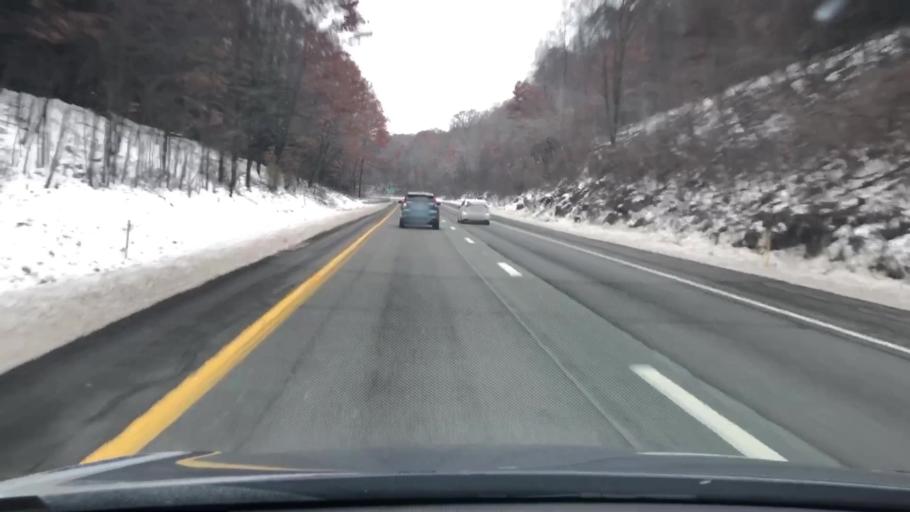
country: US
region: Pennsylvania
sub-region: Jefferson County
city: Reynoldsville
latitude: 41.1415
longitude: -78.9776
